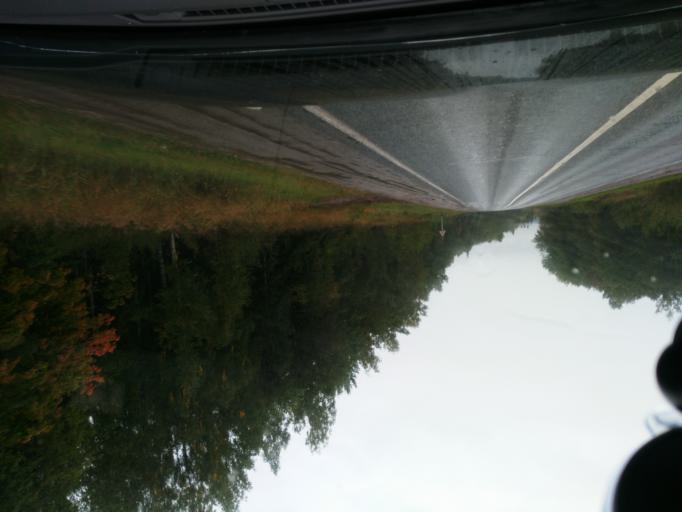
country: RU
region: Perm
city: Yugo-Kamskiy
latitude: 57.5817
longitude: 55.6773
